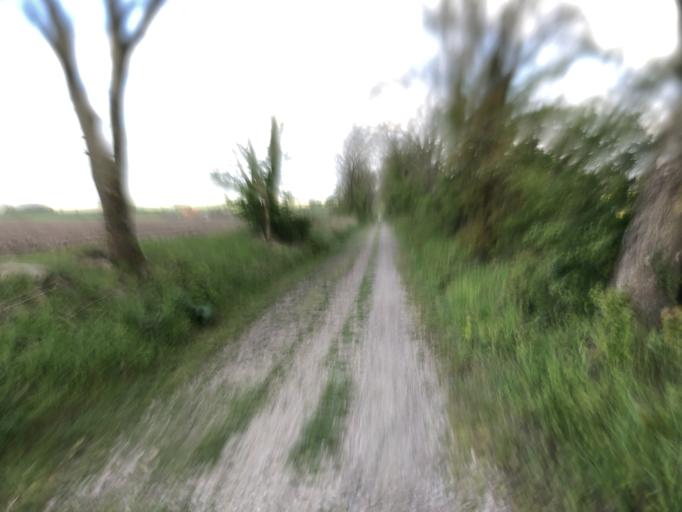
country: SE
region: Skane
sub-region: Lunds Kommun
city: Lund
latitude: 55.6972
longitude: 13.2819
